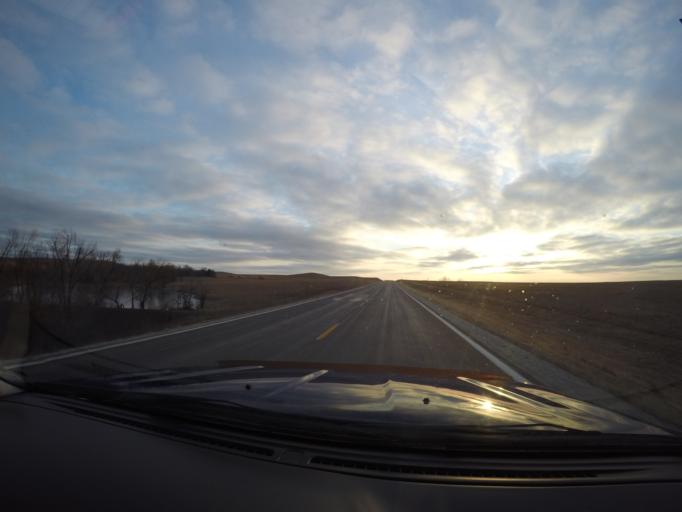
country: US
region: Kansas
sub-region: Morris County
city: Council Grove
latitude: 38.5864
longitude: -96.5105
